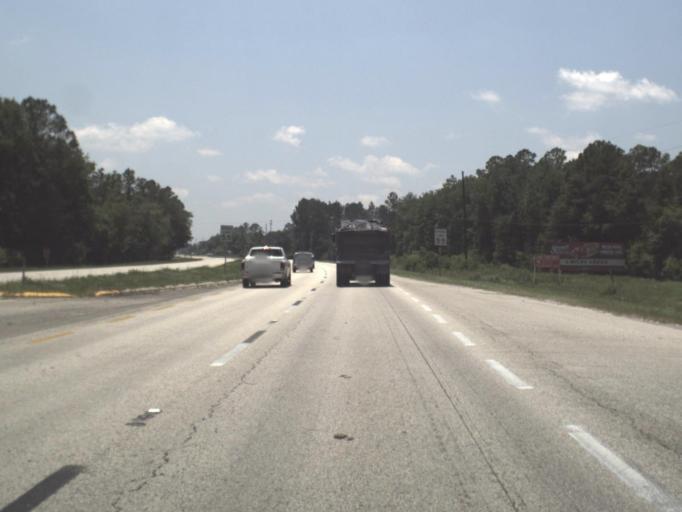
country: US
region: Florida
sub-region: Bradford County
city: Starke
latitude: 29.9832
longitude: -82.0982
